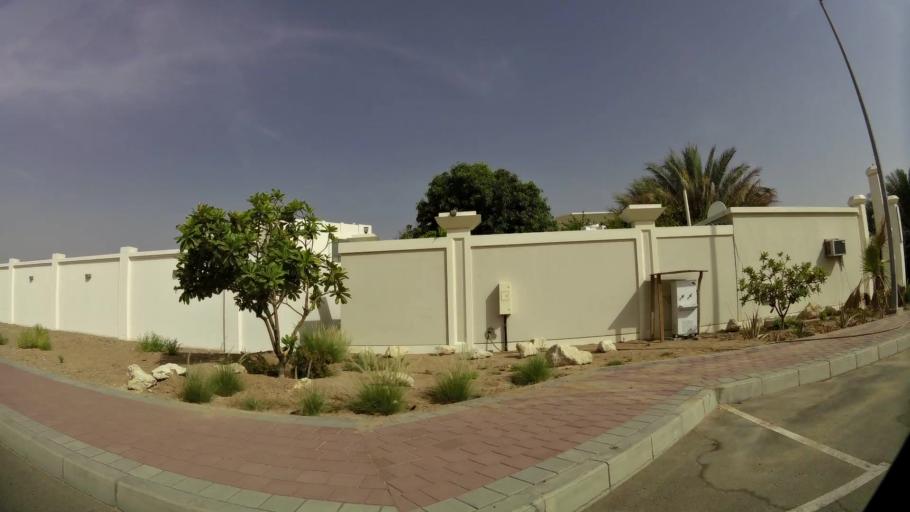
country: AE
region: Abu Dhabi
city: Al Ain
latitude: 24.1459
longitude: 55.7024
